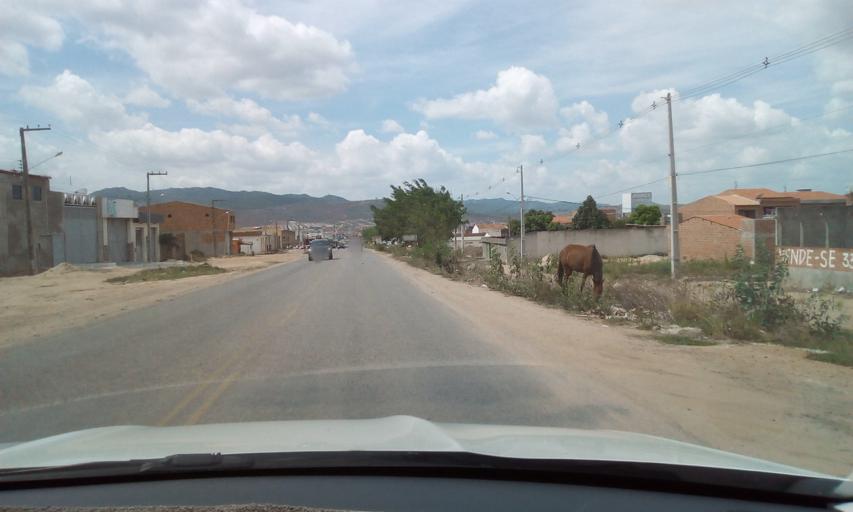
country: BR
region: Pernambuco
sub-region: Bezerros
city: Bezerros
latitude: -8.2533
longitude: -35.7579
